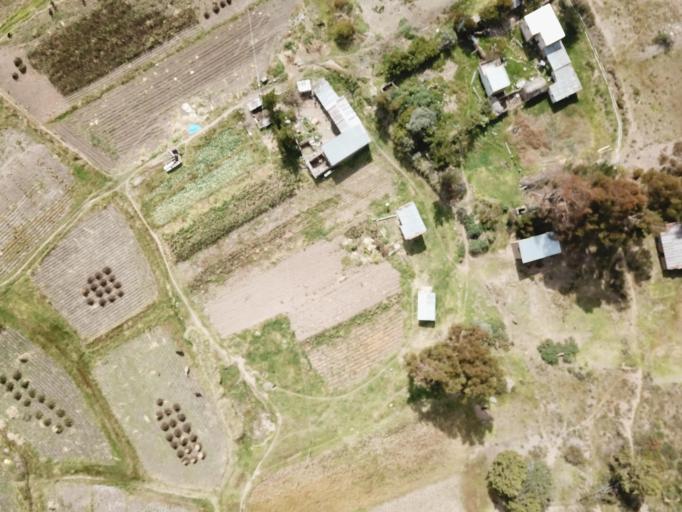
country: BO
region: La Paz
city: Achacachi
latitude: -16.0560
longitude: -68.8108
